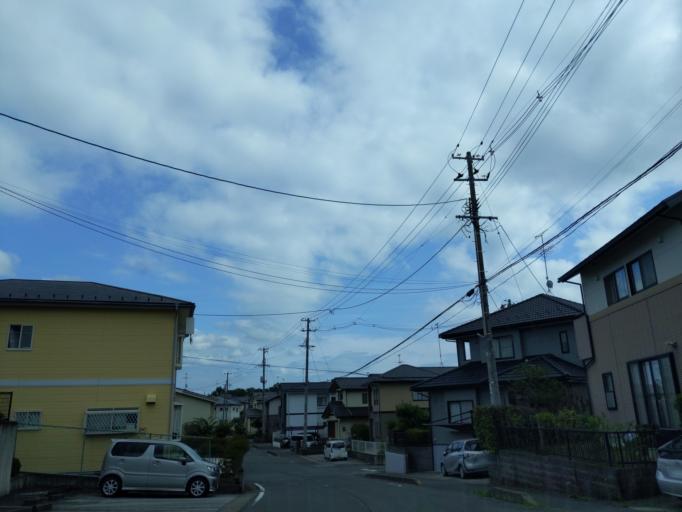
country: JP
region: Fukushima
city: Sukagawa
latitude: 37.2969
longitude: 140.3893
